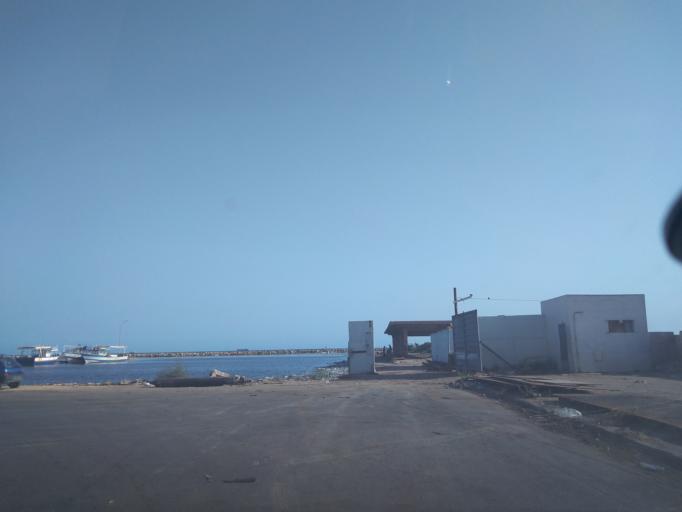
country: TN
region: Safaqis
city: Sfax
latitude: 34.7133
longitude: 10.7609
